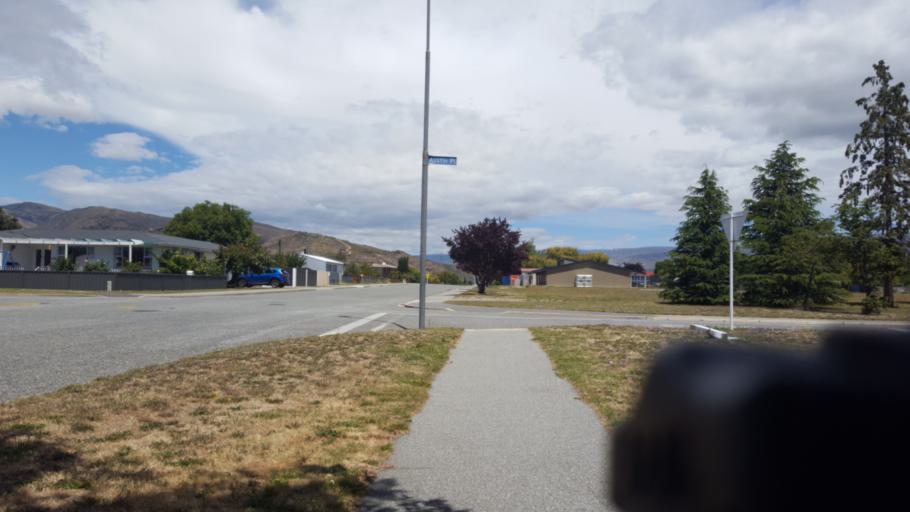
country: NZ
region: Otago
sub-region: Queenstown-Lakes District
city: Wanaka
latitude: -45.0433
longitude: 169.2052
